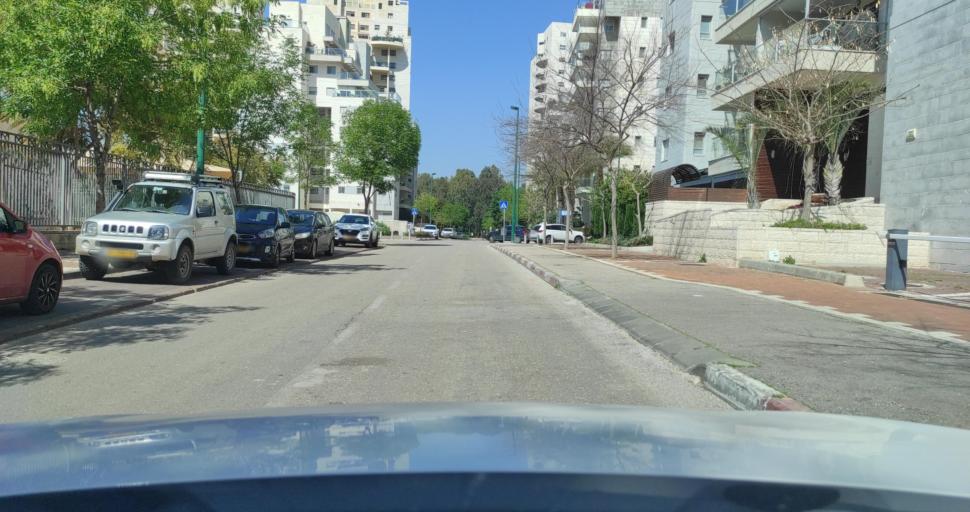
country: IL
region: Central District
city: Nordiyya
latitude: 32.3010
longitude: 34.8764
